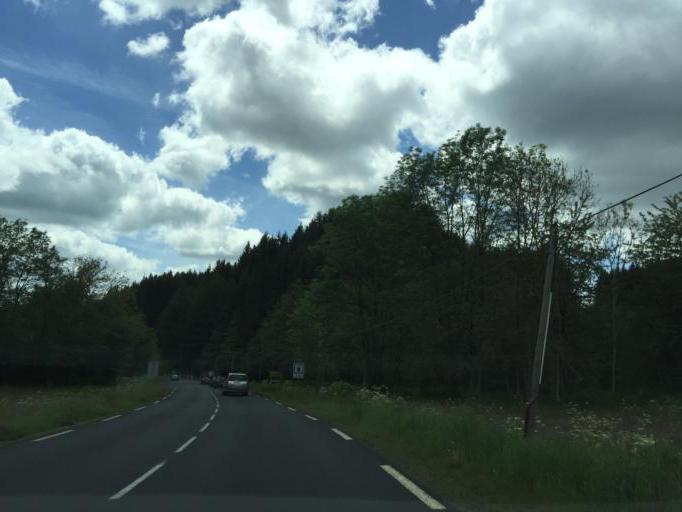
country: FR
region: Rhone-Alpes
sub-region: Departement de la Loire
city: Montbrison
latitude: 45.5350
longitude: 3.9232
